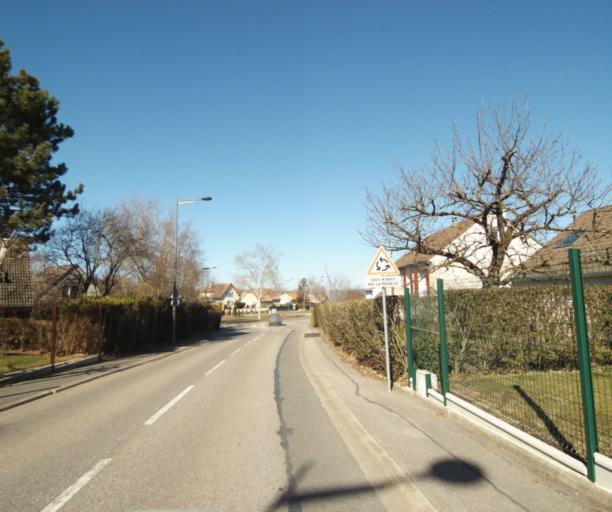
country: FR
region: Lorraine
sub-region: Departement de Meurthe-et-Moselle
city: Heillecourt
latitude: 48.6453
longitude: 6.2061
